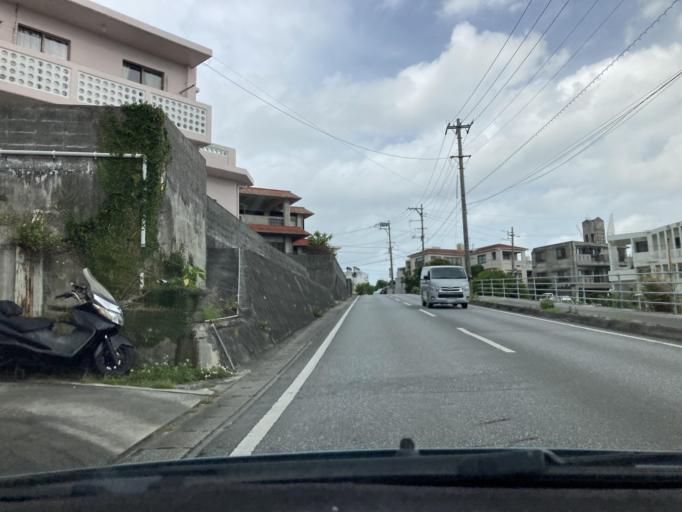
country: JP
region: Okinawa
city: Ginowan
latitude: 26.2357
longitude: 127.7388
